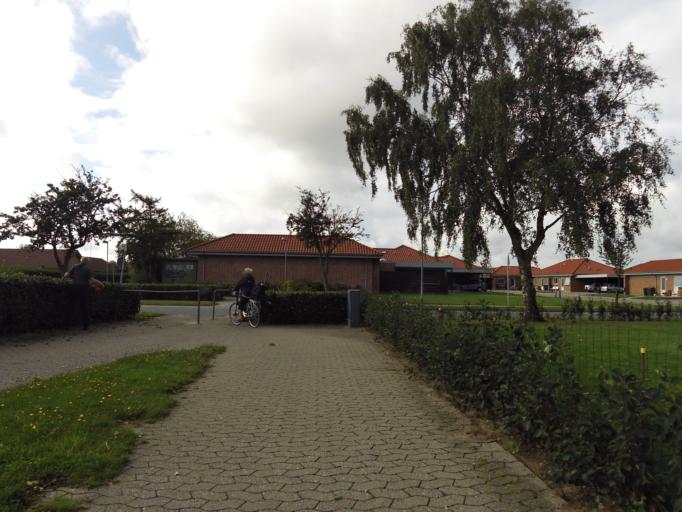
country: DK
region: South Denmark
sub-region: Esbjerg Kommune
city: Ribe
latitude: 55.3393
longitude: 8.7816
